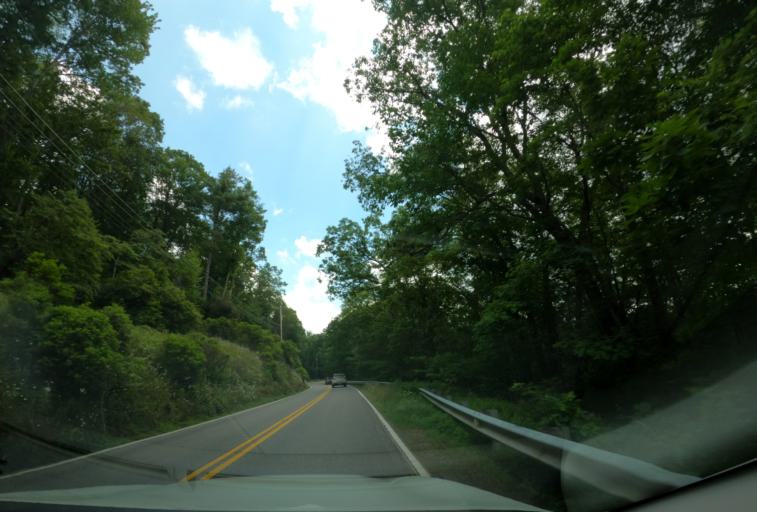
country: US
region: North Carolina
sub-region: Jackson County
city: Cullowhee
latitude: 35.0873
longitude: -83.1639
